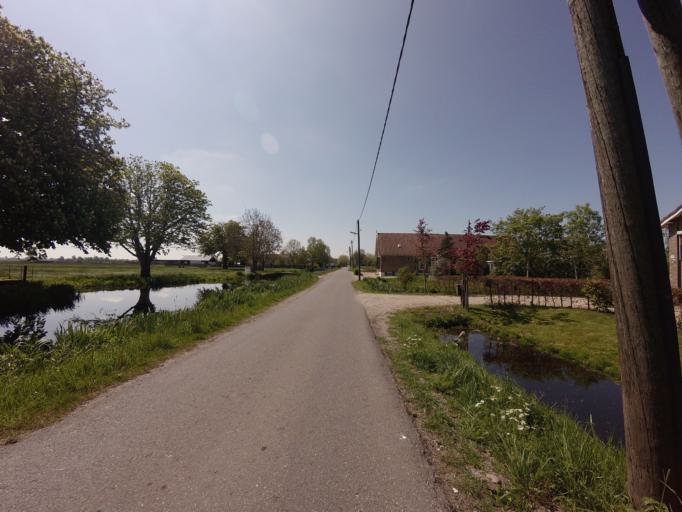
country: NL
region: South Holland
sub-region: Gemeente Gouda
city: Gouda
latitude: 51.9731
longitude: 4.7057
